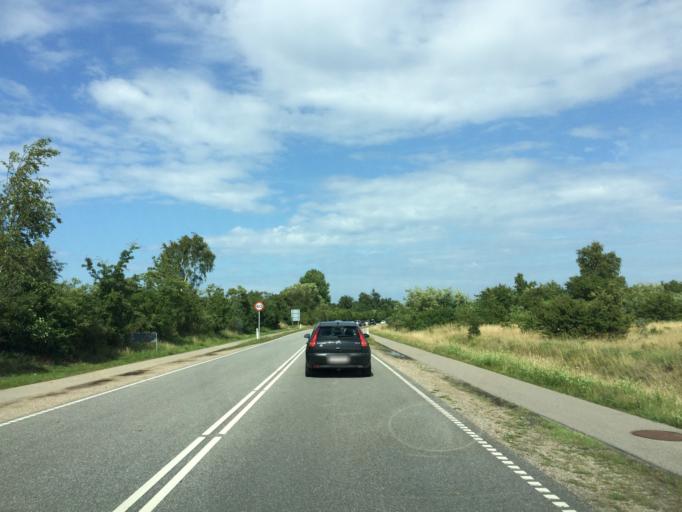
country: DK
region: Zealand
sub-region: Odsherred Kommune
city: Asnaes
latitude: 55.9791
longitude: 11.3032
